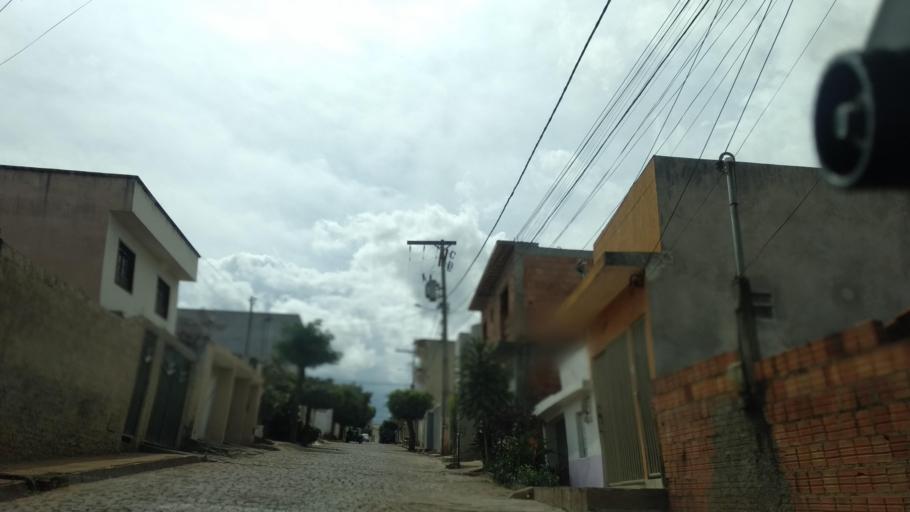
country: BR
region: Bahia
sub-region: Caetite
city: Caetite
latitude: -14.0635
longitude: -42.4815
